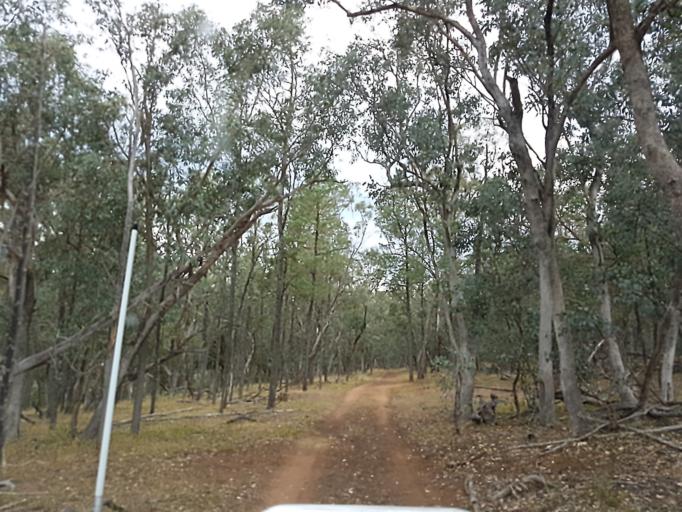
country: AU
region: New South Wales
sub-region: Snowy River
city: Jindabyne
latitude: -36.9564
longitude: 148.4086
